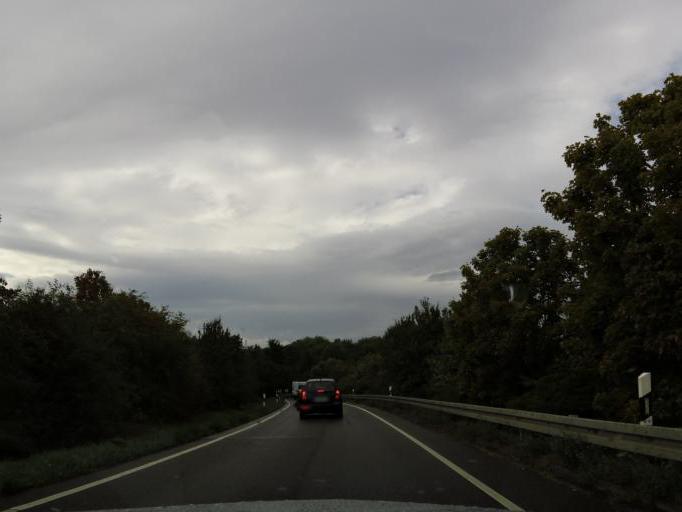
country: DE
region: Hesse
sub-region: Regierungsbezirk Darmstadt
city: Steinbach am Taunus
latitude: 50.1678
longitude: 8.6312
